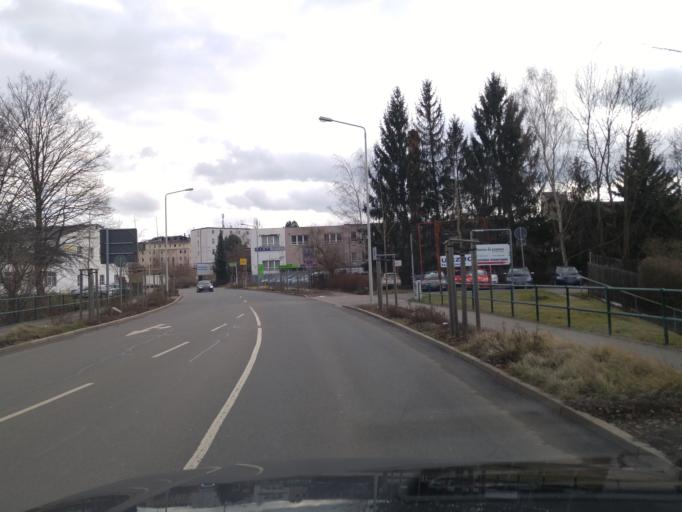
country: DE
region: Saxony
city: Zwickau
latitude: 50.7197
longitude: 12.4768
